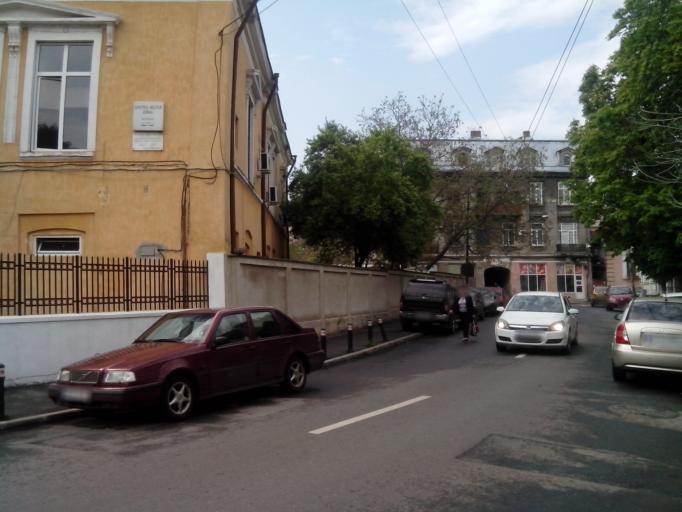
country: RO
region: Bucuresti
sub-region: Municipiul Bucuresti
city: Bucuresti
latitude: 44.4249
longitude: 26.0954
